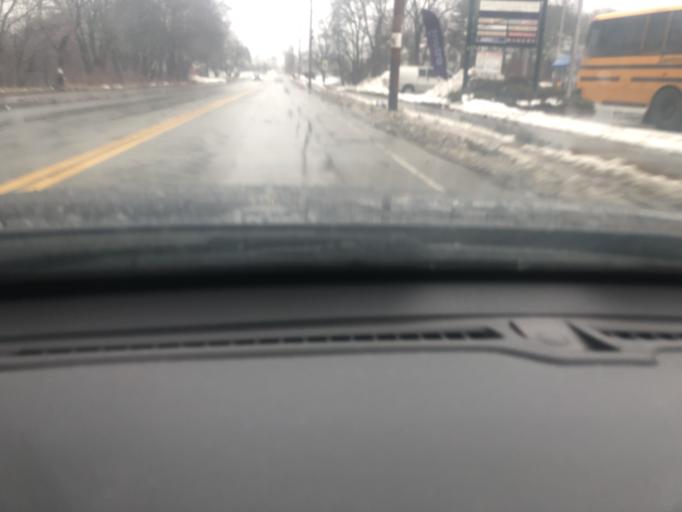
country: US
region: Massachusetts
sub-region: Plymouth County
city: Brockton
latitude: 42.1017
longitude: -71.0331
